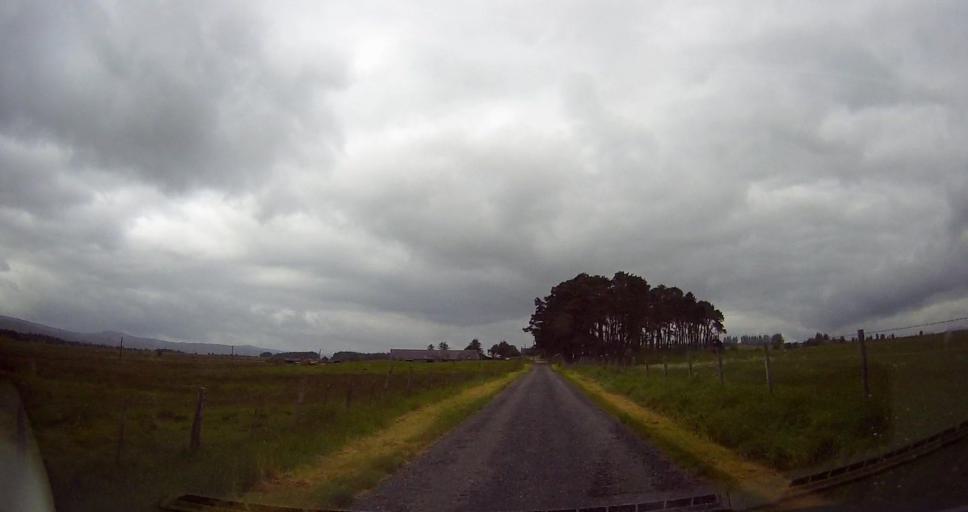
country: GB
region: Scotland
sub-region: Highland
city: Alness
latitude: 58.0700
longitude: -4.4302
